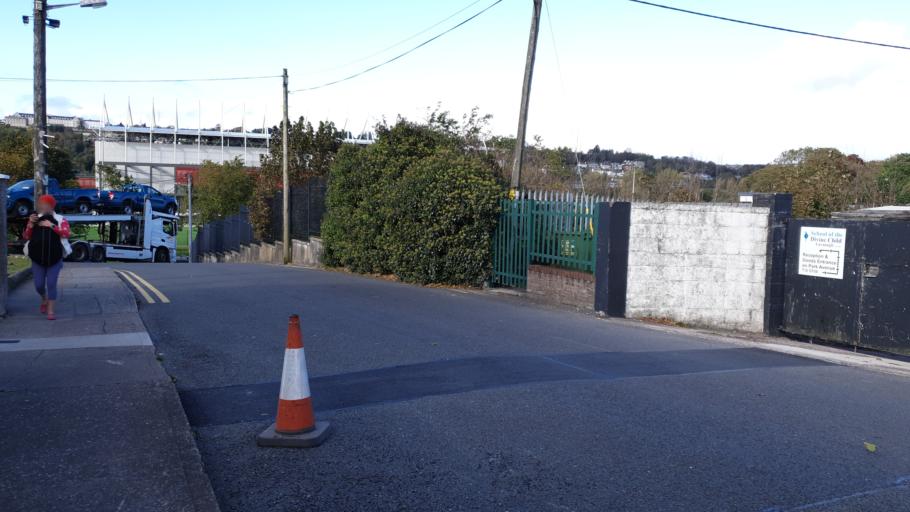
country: IE
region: Munster
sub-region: County Cork
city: Cork
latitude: 51.8966
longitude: -8.4343
